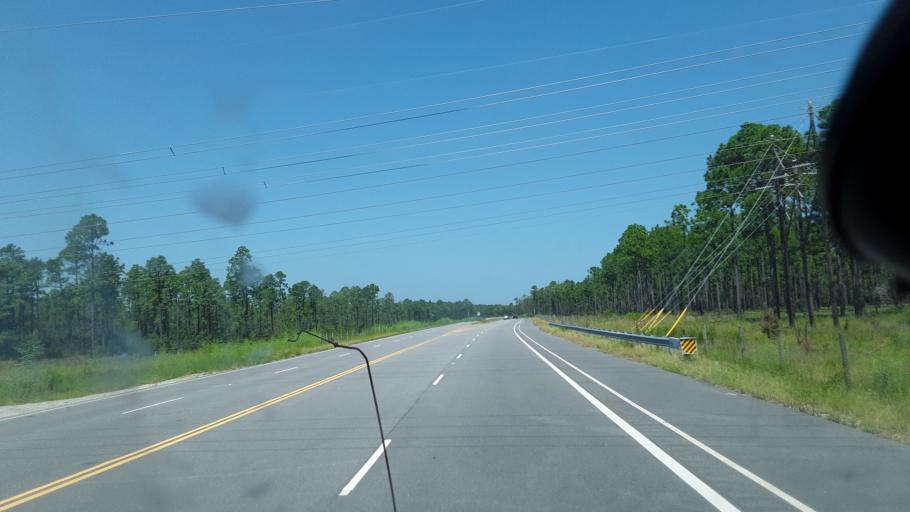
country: US
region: South Carolina
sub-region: Horry County
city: Myrtle Beach
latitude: 33.7861
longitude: -78.8779
